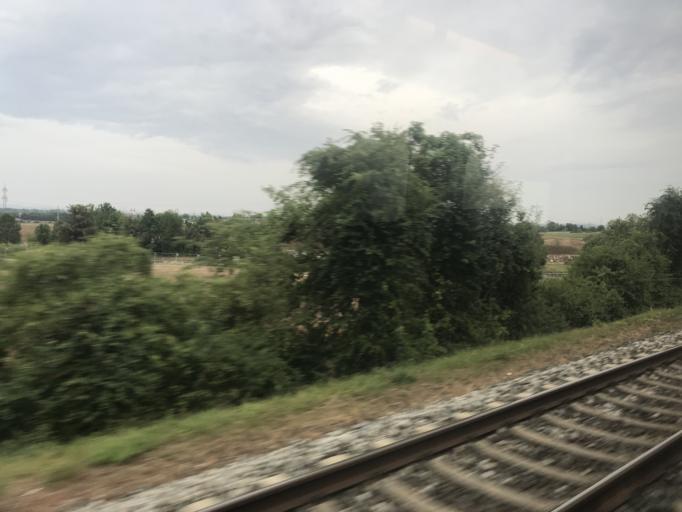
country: DE
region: Bavaria
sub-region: Regierungsbezirk Unterfranken
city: Bergrheinfeld
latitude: 50.0236
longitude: 10.1722
